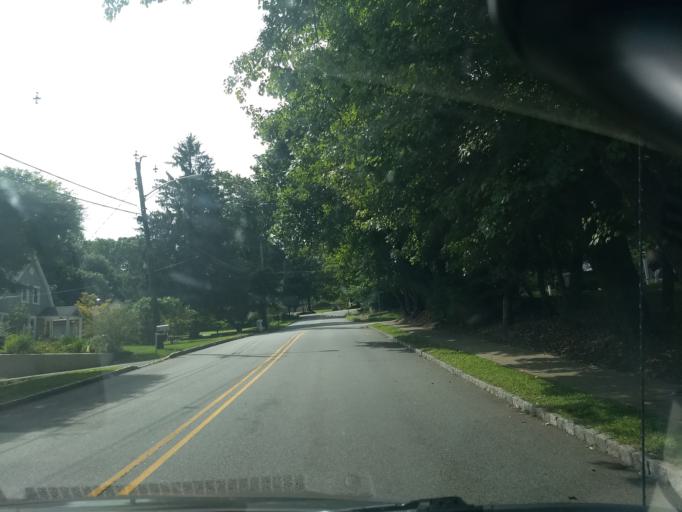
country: US
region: New Jersey
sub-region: Morris County
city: Morristown
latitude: 40.8089
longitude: -74.4963
